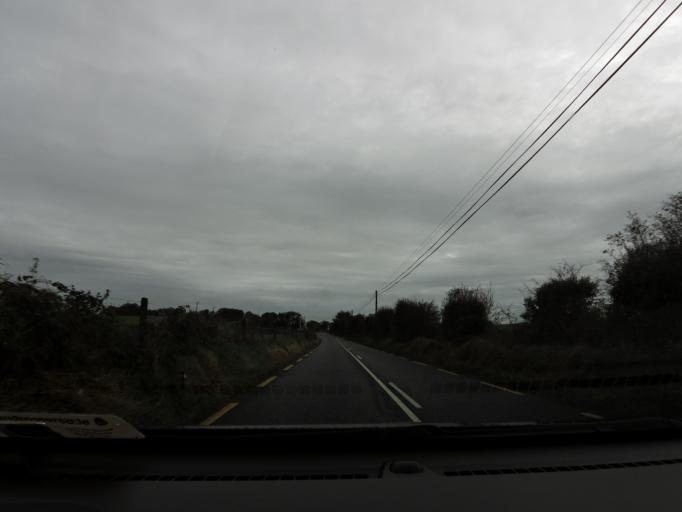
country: IE
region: Connaught
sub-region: County Galway
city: Tuam
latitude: 53.5934
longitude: -8.7714
